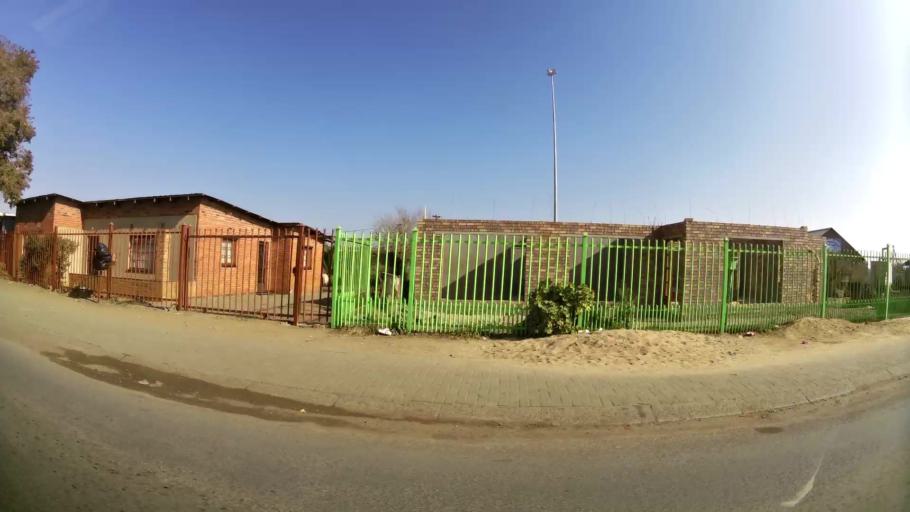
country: ZA
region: Orange Free State
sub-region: Mangaung Metropolitan Municipality
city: Bloemfontein
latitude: -29.1471
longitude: 26.2405
